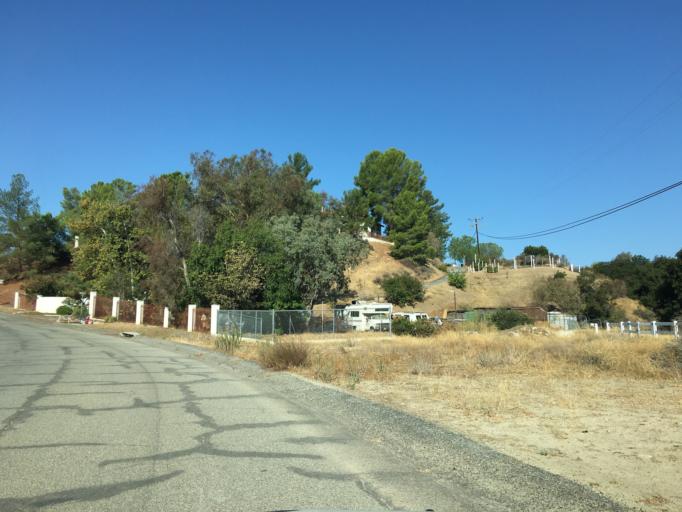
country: US
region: California
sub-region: Los Angeles County
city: Val Verde
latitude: 34.4744
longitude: -118.6672
